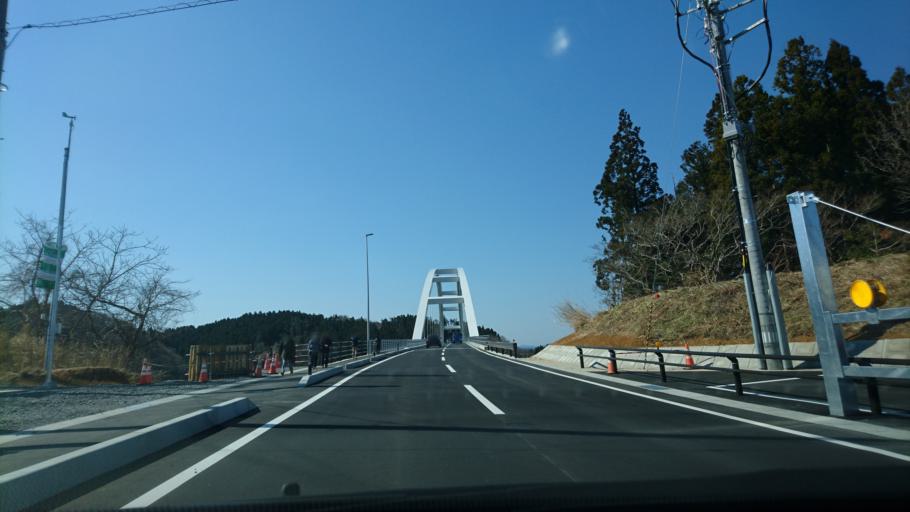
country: JP
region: Iwate
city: Ofunato
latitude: 38.8808
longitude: 141.6071
